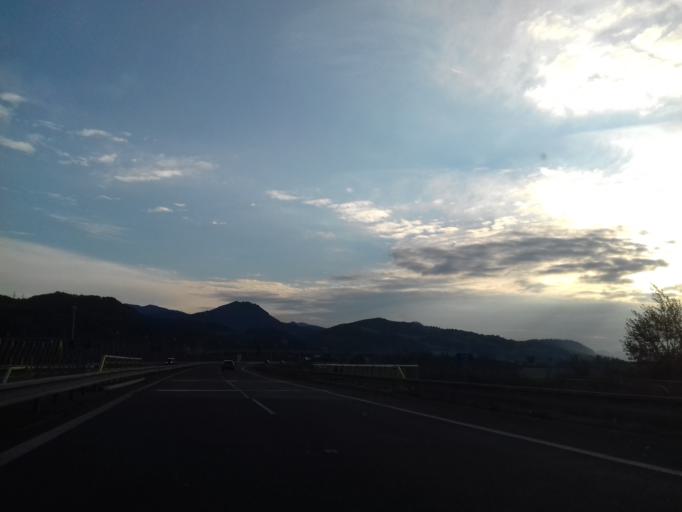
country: SK
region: Zilinsky
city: Bytca
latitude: 49.2399
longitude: 18.6411
